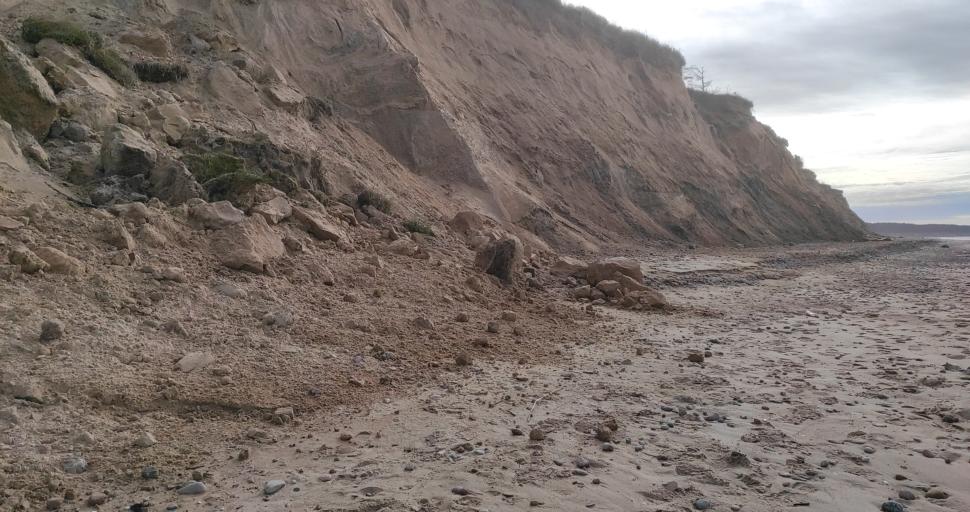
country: LV
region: Alsunga
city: Alsunga
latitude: 57.0420
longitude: 21.4041
